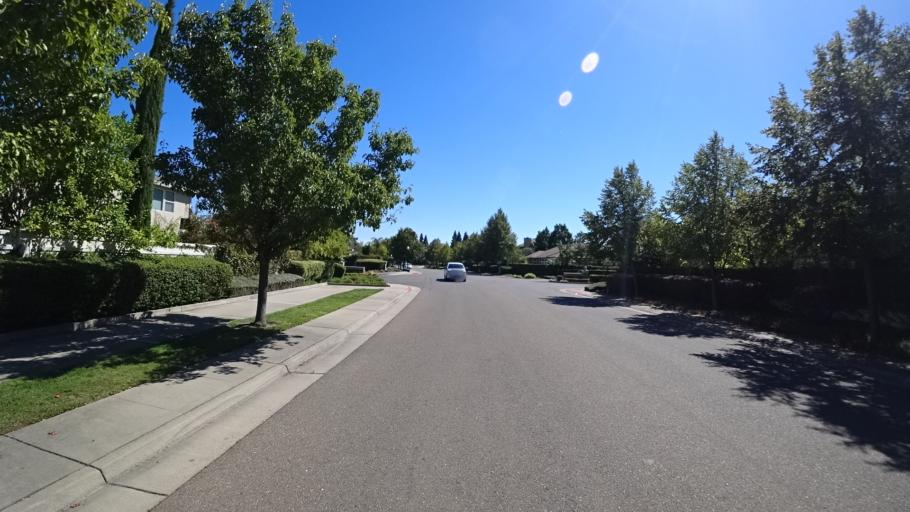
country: US
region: California
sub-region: Sacramento County
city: Laguna
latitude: 38.4113
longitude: -121.4683
